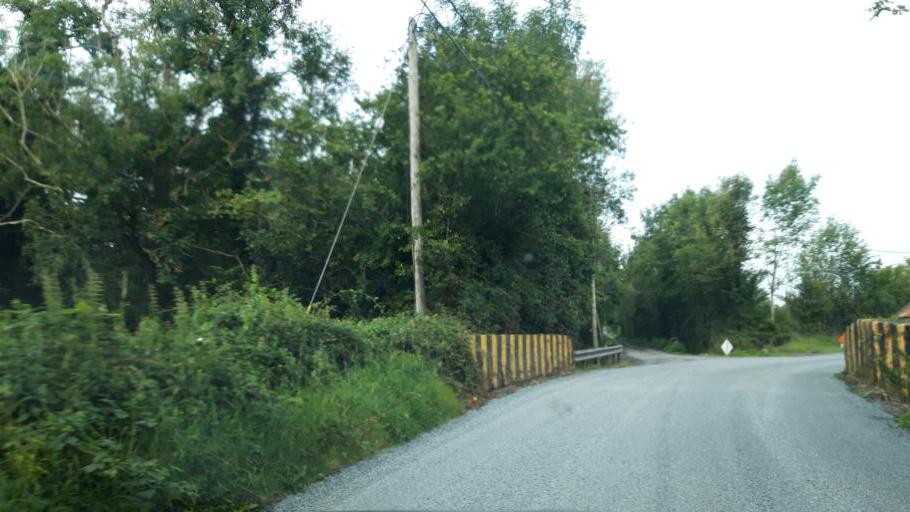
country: IE
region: Leinster
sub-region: Kilkenny
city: Callan
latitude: 52.5338
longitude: -7.5202
